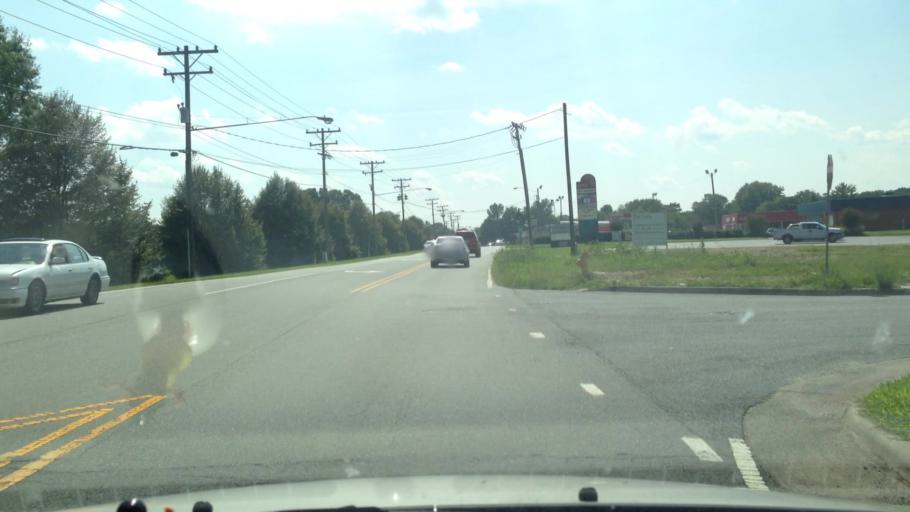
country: US
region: North Carolina
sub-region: Forsyth County
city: Kernersville
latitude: 36.1284
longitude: -80.0622
